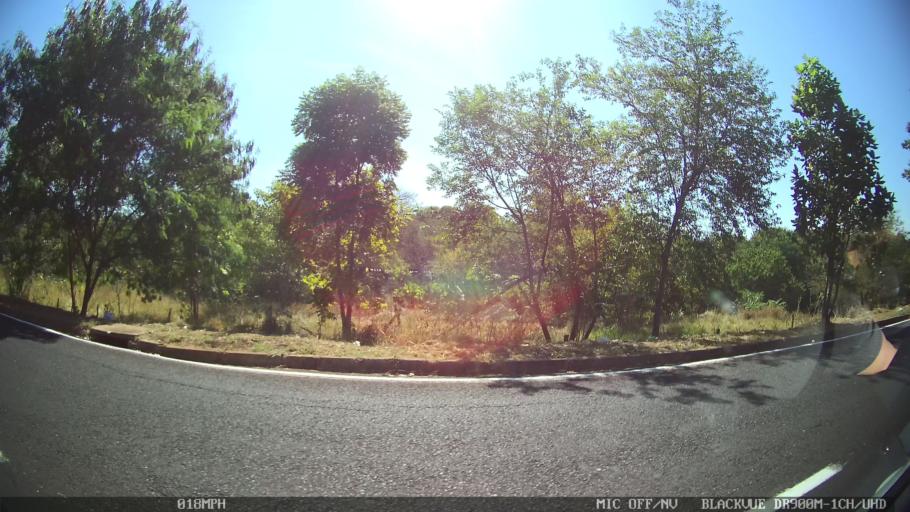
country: BR
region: Sao Paulo
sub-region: Sao Jose Do Rio Preto
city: Sao Jose do Rio Preto
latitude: -20.7734
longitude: -49.4045
